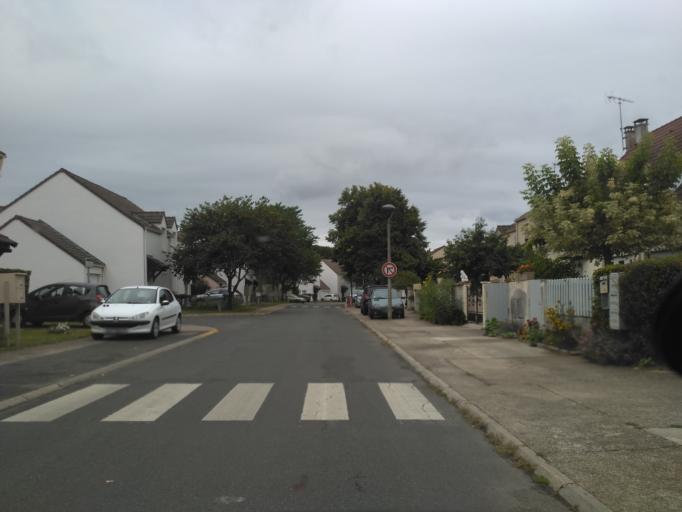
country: FR
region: Ile-de-France
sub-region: Departement de Seine-et-Marne
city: Vert-Saint-Denis
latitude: 48.5609
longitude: 2.6278
